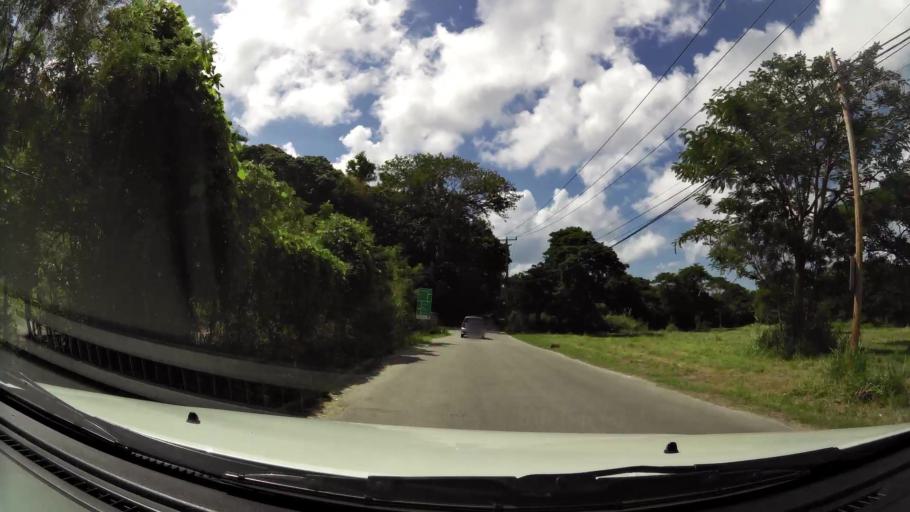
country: BB
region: Saint James
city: Holetown
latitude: 13.1972
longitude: -59.6364
